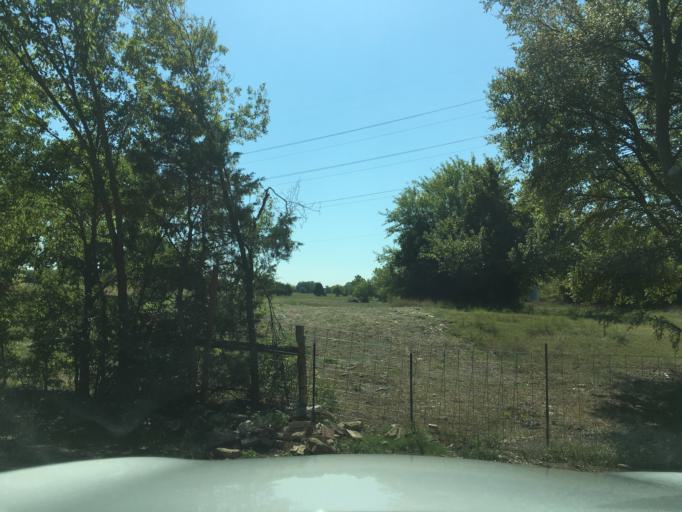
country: US
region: Texas
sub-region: Dallas County
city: Sachse
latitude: 32.9604
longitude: -96.6099
